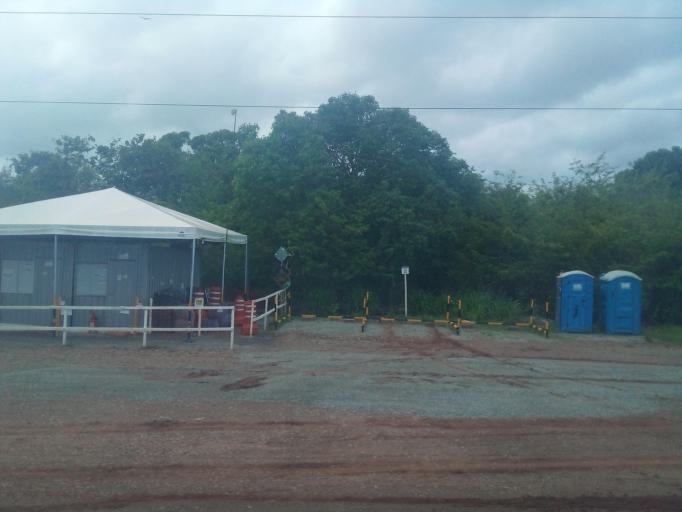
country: BR
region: Maranhao
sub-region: Arari
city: Arari
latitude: -3.5717
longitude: -44.6889
